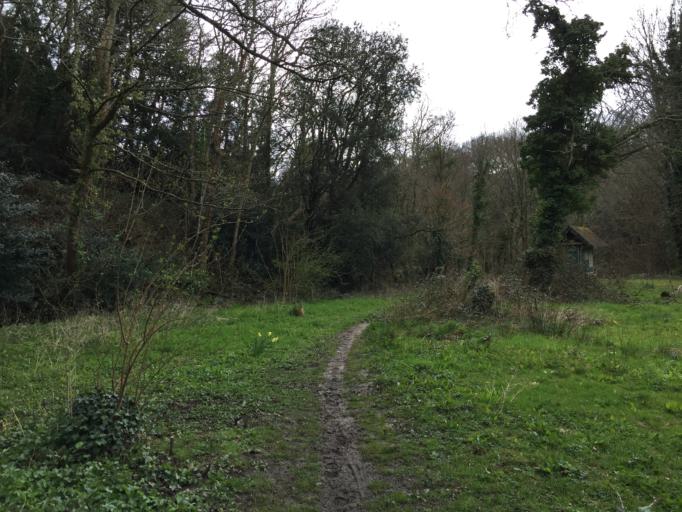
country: JE
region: St Helier
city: Saint Helier
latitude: 49.2131
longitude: -2.1341
